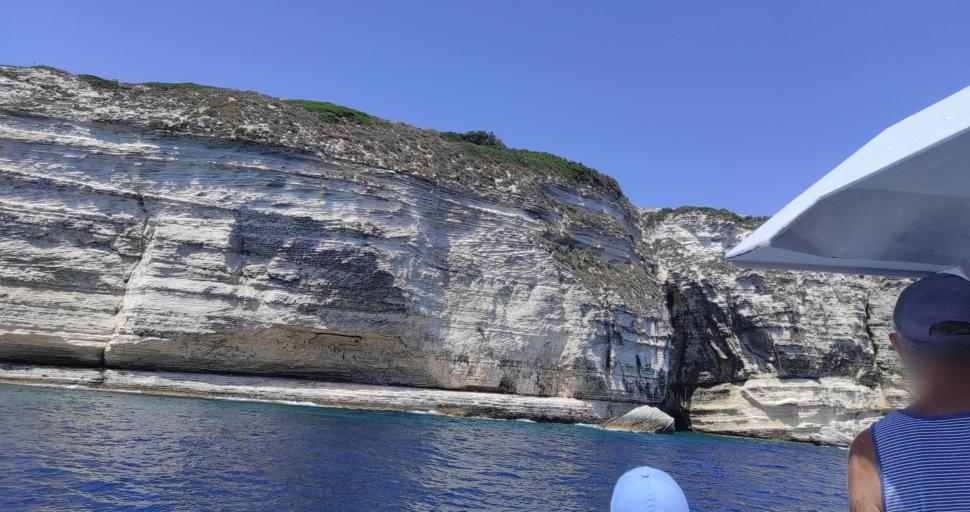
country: FR
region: Corsica
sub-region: Departement de la Corse-du-Sud
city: Bonifacio
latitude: 41.3850
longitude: 9.1518
